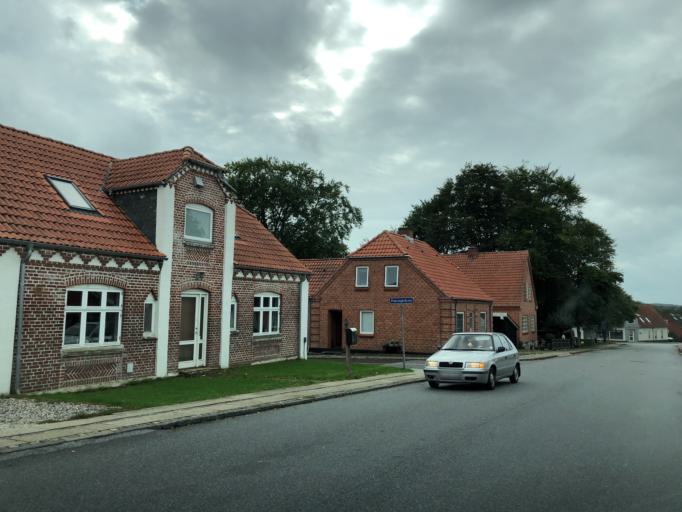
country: DK
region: Central Jutland
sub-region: Herning Kommune
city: Vildbjerg
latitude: 56.1768
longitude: 8.7434
